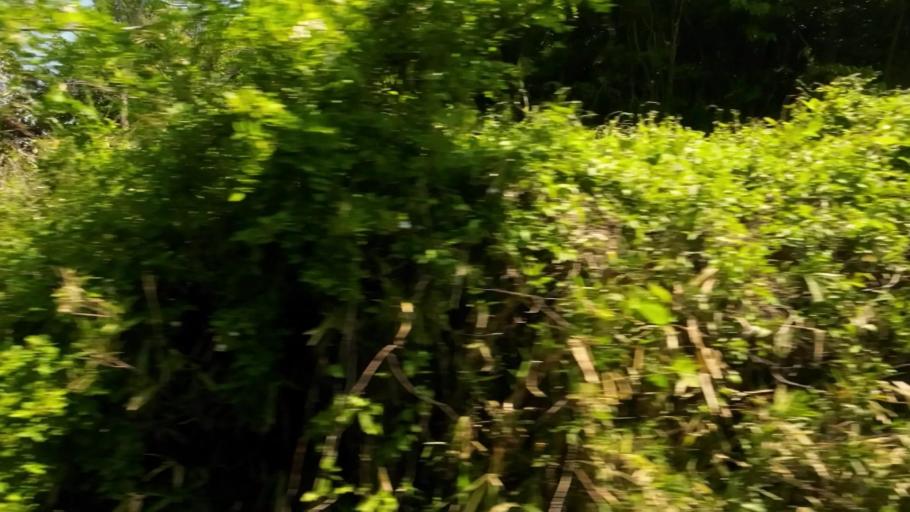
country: JP
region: Ehime
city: Hojo
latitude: 34.0617
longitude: 132.9051
